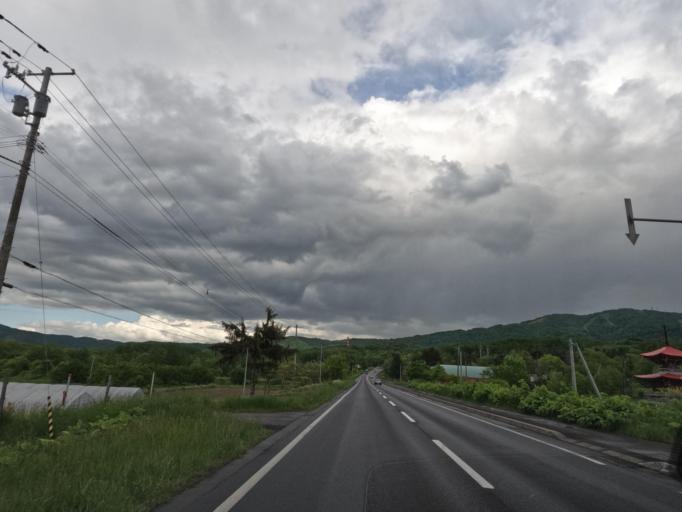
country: JP
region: Hokkaido
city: Fukagawa
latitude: 43.7129
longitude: 142.1628
